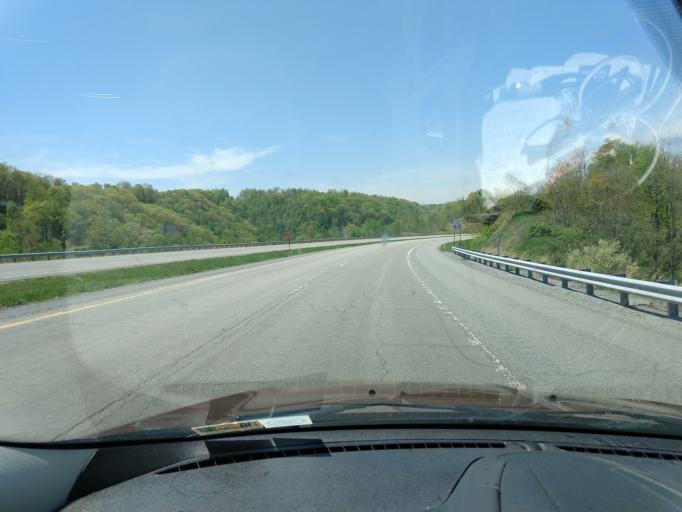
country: US
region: West Virginia
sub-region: Raleigh County
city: Sophia
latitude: 37.7121
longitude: -81.2910
